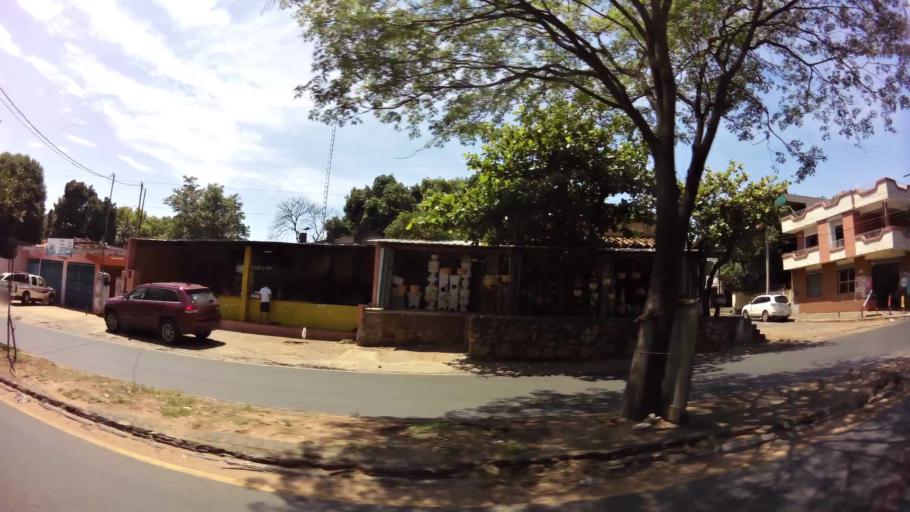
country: PY
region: Central
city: San Lorenzo
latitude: -25.3590
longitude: -57.5147
